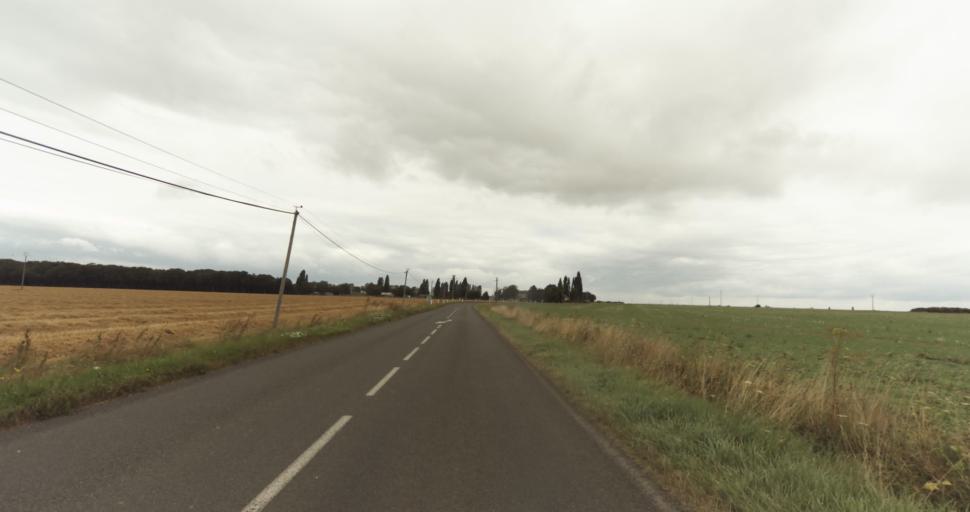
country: FR
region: Haute-Normandie
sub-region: Departement de l'Eure
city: Gravigny
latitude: 49.0408
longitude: 1.2107
